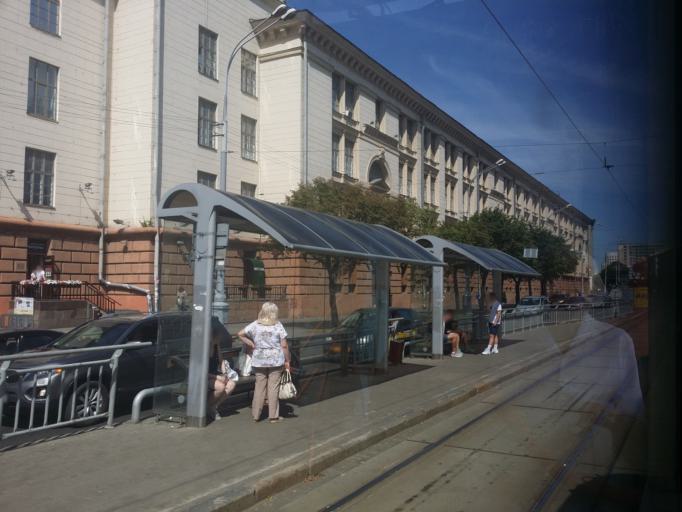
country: BY
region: Minsk
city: Minsk
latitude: 53.9165
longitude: 27.5832
